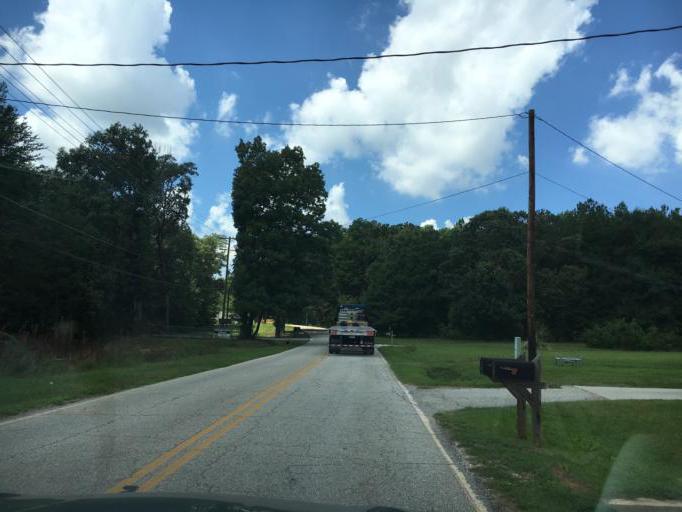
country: US
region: South Carolina
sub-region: Spartanburg County
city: Duncan
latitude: 34.9018
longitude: -82.1387
